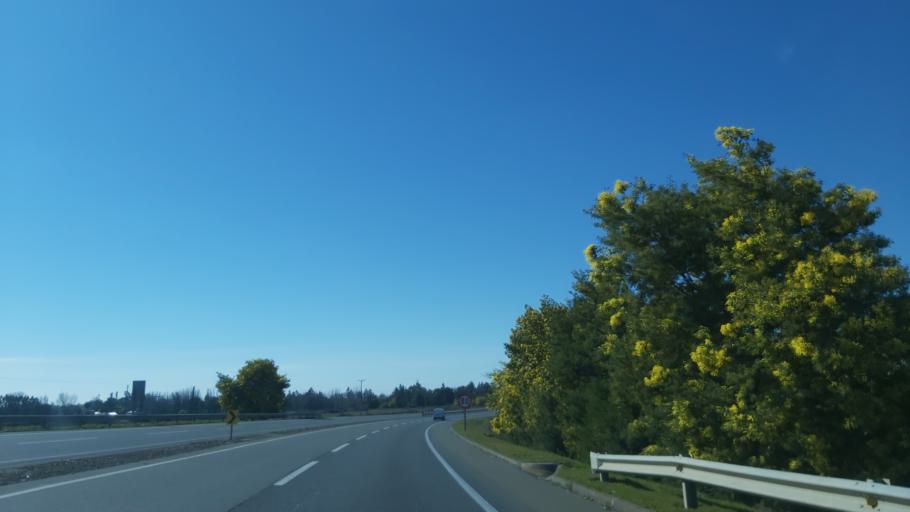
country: CL
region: Biobio
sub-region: Provincia de Nuble
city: Bulnes
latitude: -36.6540
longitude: -72.2388
